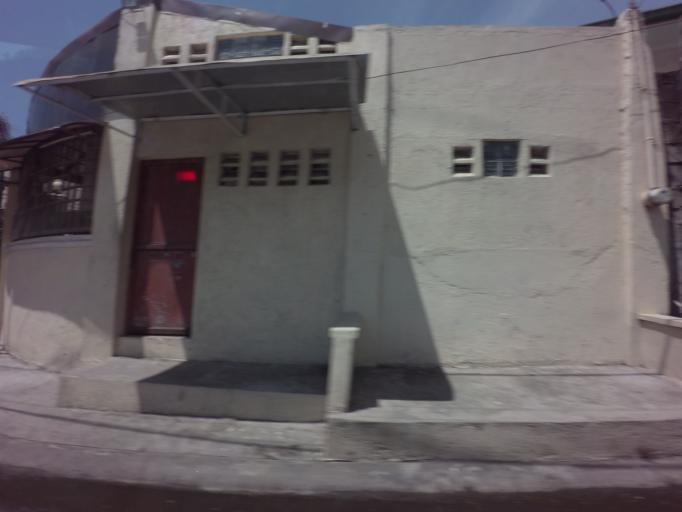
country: PH
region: Calabarzon
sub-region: Province of Rizal
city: Las Pinas
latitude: 14.4267
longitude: 120.9873
